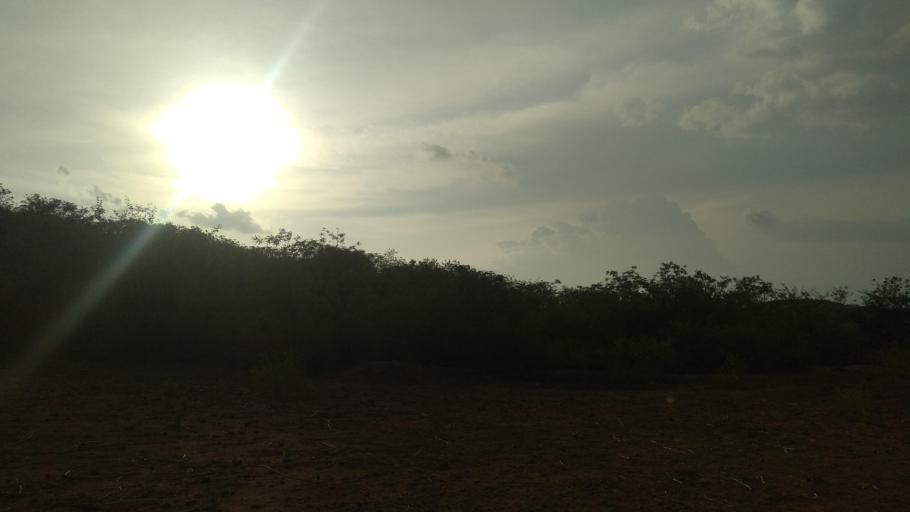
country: IN
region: Telangana
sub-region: Mahbubnagar
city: Farrukhnagar
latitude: 16.8900
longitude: 78.4834
